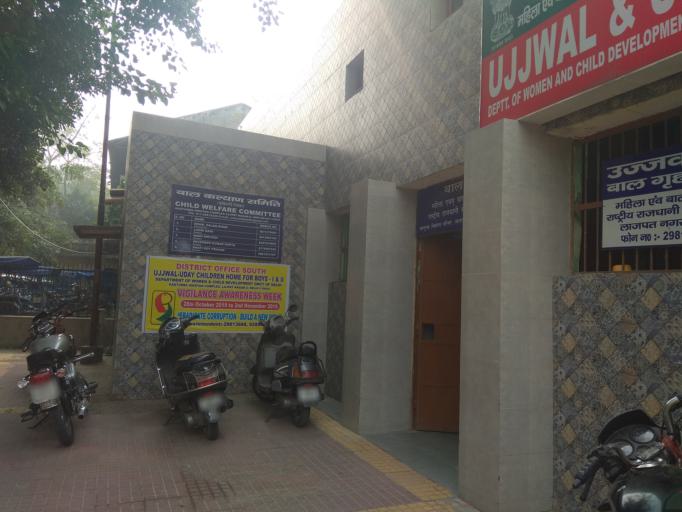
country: IN
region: NCT
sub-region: New Delhi
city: New Delhi
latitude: 28.5719
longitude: 77.2448
